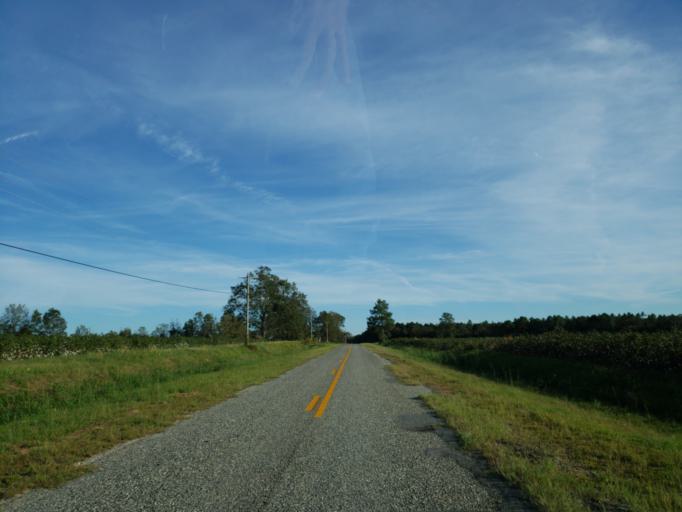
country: US
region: Georgia
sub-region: Crisp County
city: Cordele
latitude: 32.0259
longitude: -83.7417
